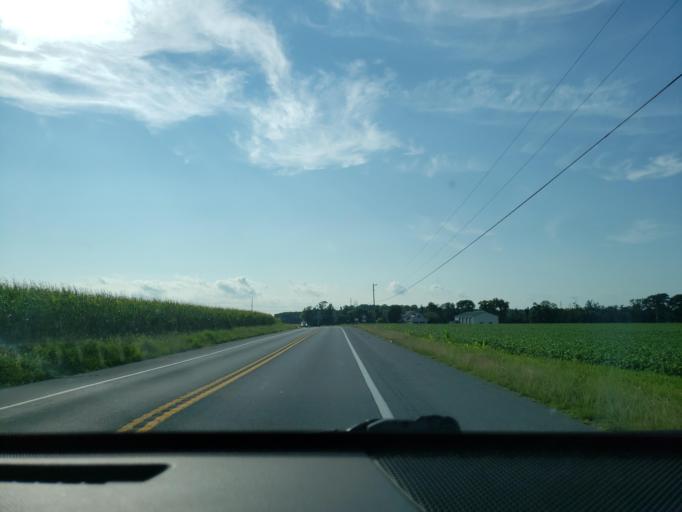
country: US
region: Delaware
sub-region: Sussex County
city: Milton
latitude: 38.7631
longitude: -75.2705
